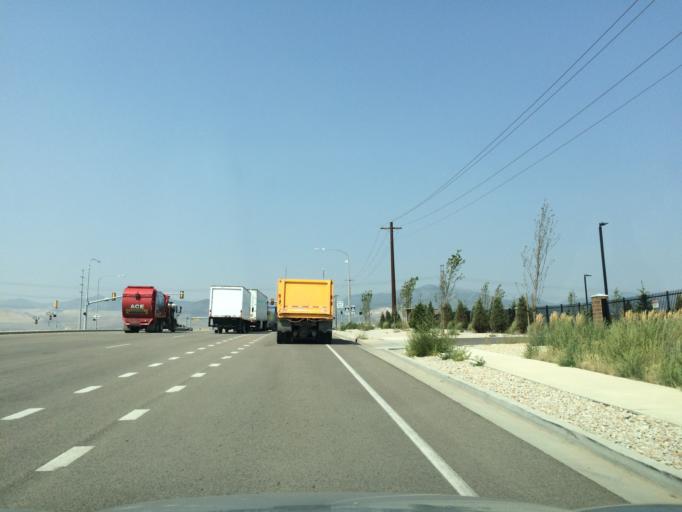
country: US
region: Utah
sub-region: Salt Lake County
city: Oquirrh
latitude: 40.5880
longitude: -112.0262
